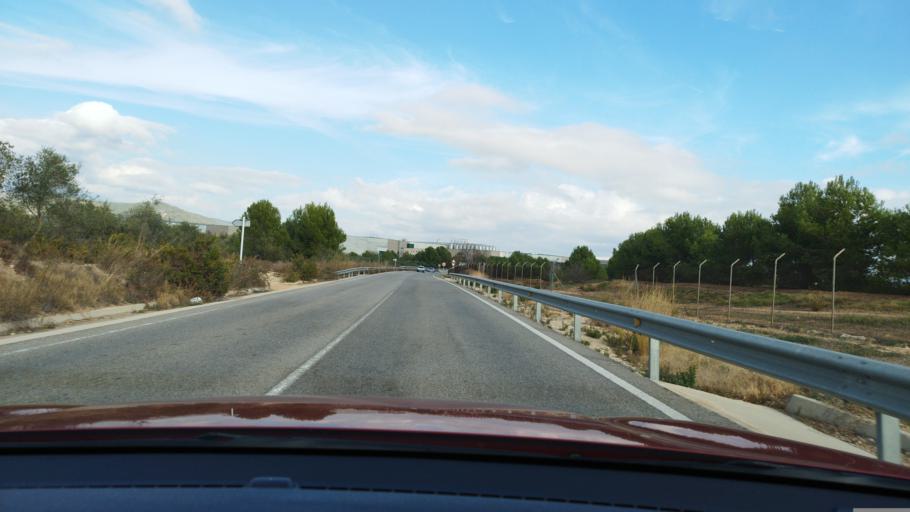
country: ES
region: Catalonia
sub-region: Provincia de Tarragona
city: la Bisbal del Penedes
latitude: 41.2675
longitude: 1.5013
